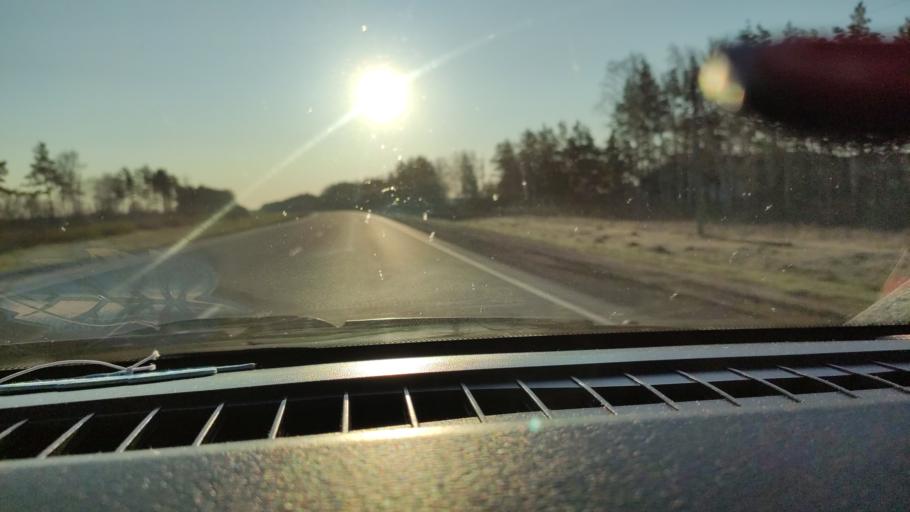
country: RU
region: Saratov
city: Sennoy
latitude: 52.1516
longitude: 46.9974
